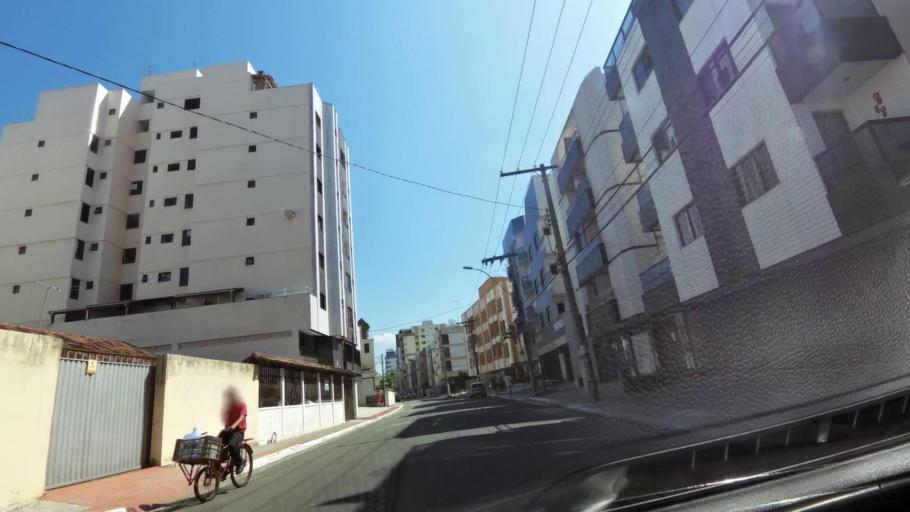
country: BR
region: Espirito Santo
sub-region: Guarapari
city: Guarapari
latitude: -20.6508
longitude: -40.4808
